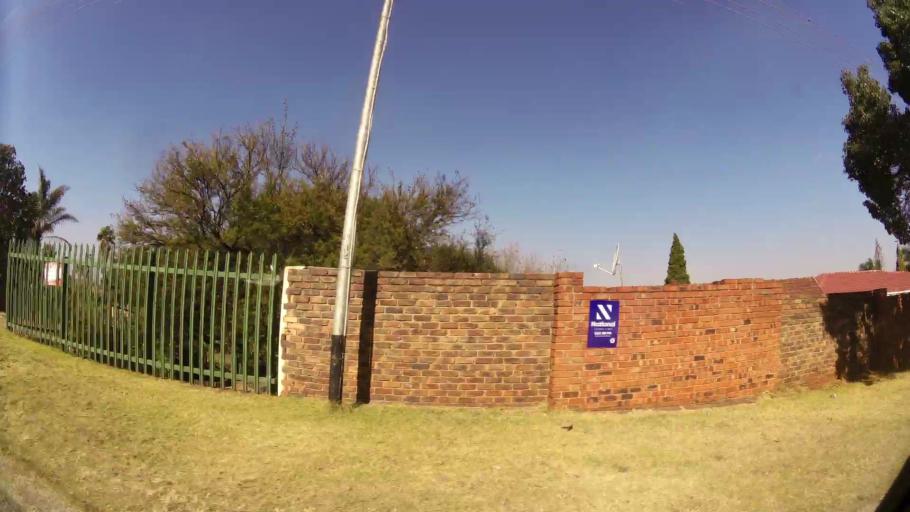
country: ZA
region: Gauteng
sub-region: City of Johannesburg Metropolitan Municipality
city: Johannesburg
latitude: -26.2623
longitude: 28.0518
